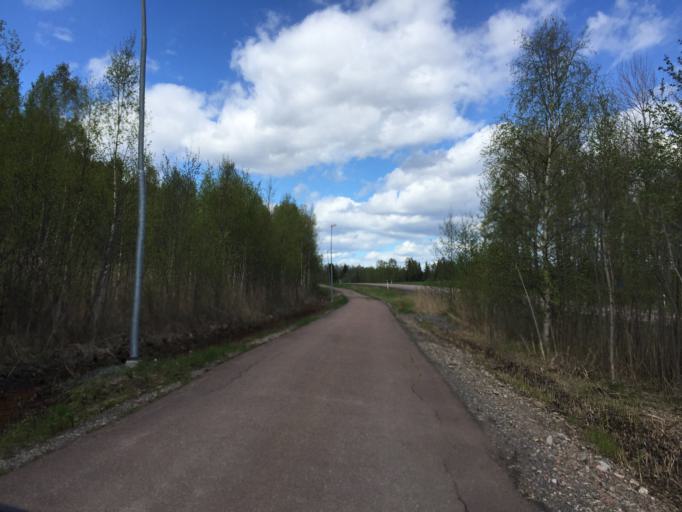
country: SE
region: Dalarna
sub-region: Ludvika Kommun
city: Ludvika
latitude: 60.1883
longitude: 15.2109
